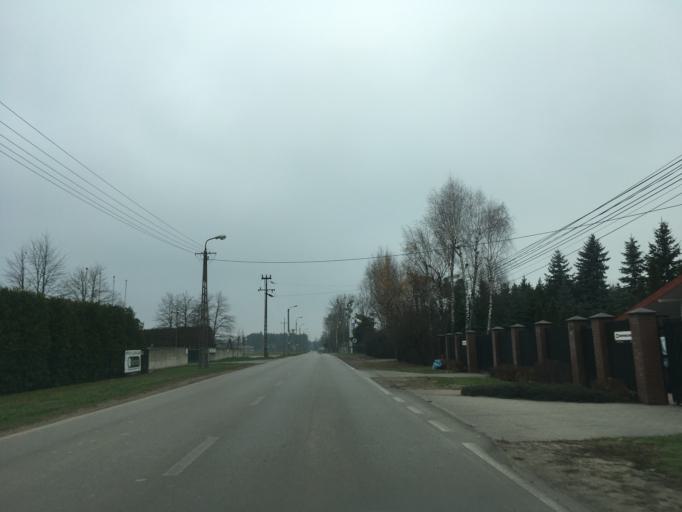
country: PL
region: Masovian Voivodeship
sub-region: Powiat piaseczynski
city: Lesznowola
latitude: 52.0695
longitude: 20.9425
